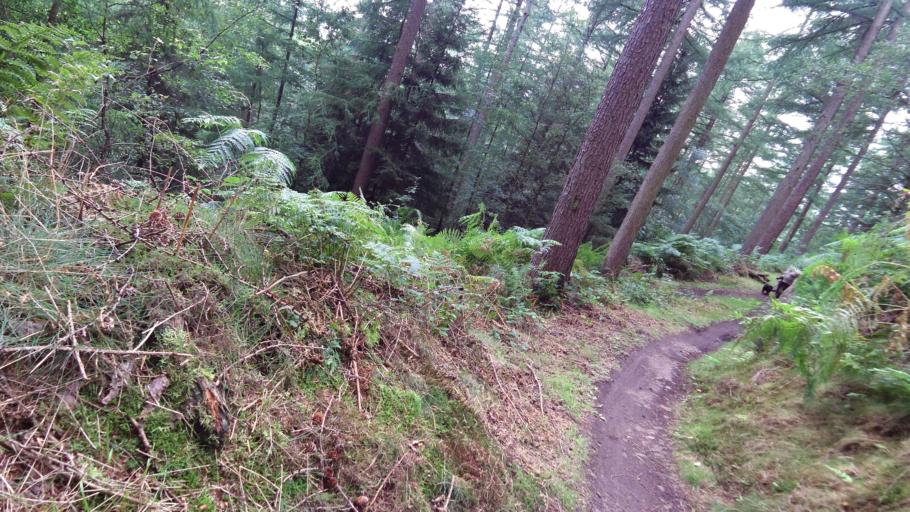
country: GB
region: England
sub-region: North Yorkshire
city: Thornton Dale
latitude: 54.2807
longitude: -0.6856
